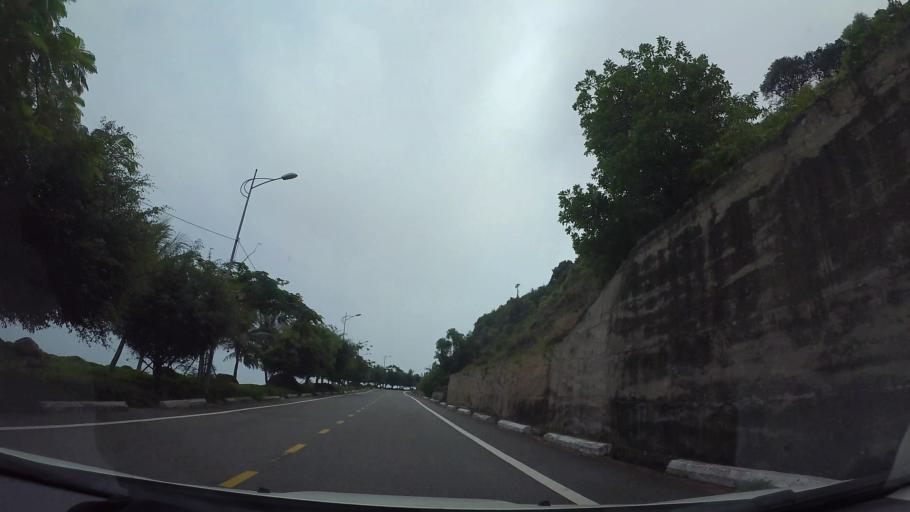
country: VN
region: Da Nang
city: Son Tra
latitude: 16.1041
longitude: 108.3076
